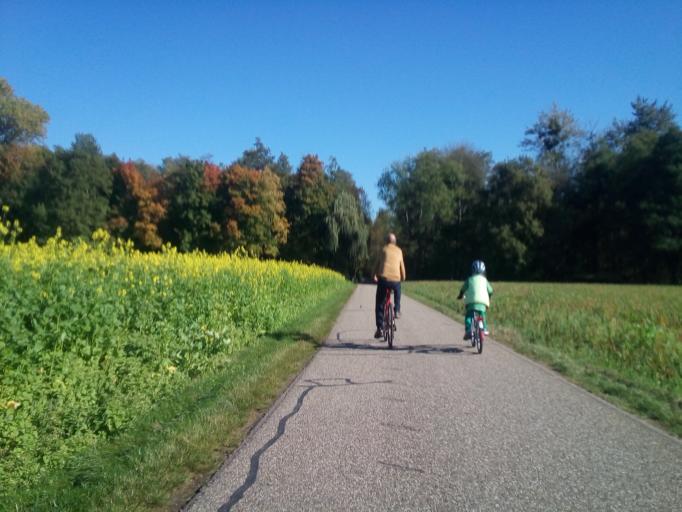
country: DE
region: Baden-Wuerttemberg
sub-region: Karlsruhe Region
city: Zell
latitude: 48.6889
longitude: 8.0387
